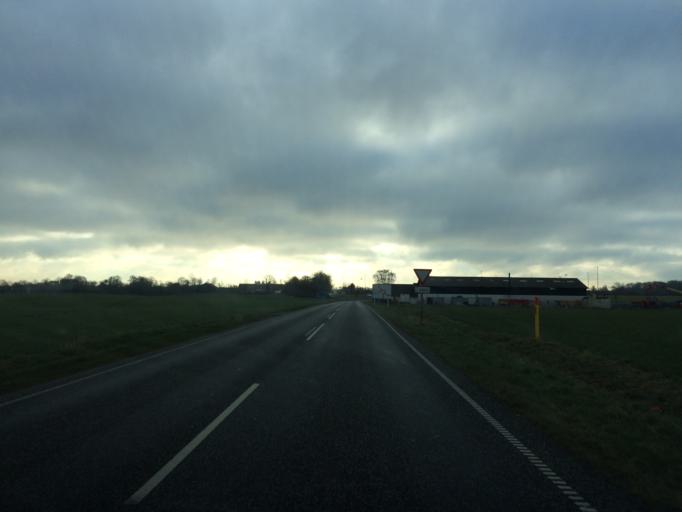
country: DK
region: South Denmark
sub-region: Fredericia Kommune
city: Snoghoj
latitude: 55.5686
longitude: 9.6857
